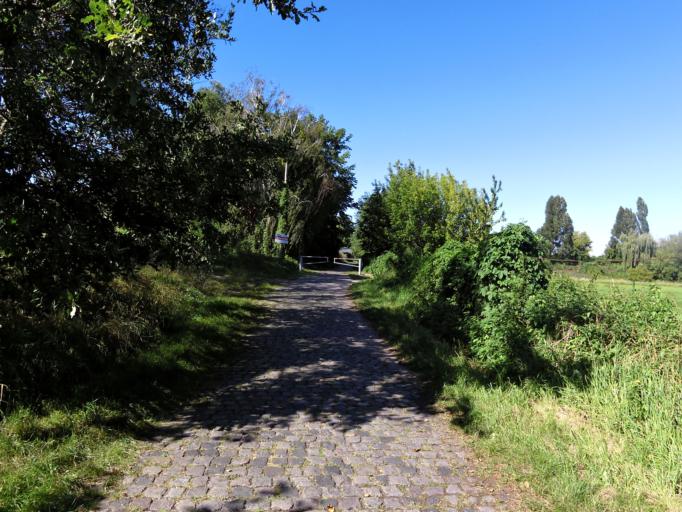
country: DE
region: Saxony-Anhalt
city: Wittenburg
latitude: 51.8623
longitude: 12.6795
